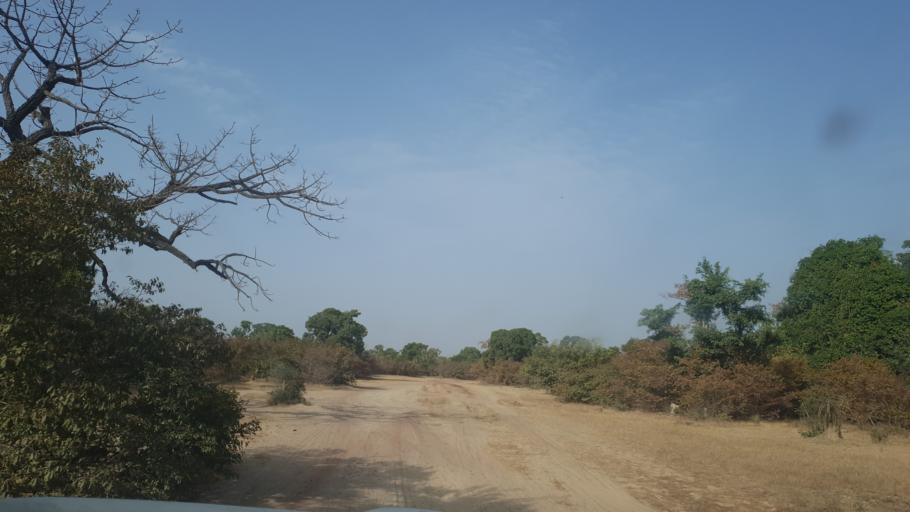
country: ML
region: Segou
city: Baroueli
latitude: 13.3679
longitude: -6.9169
